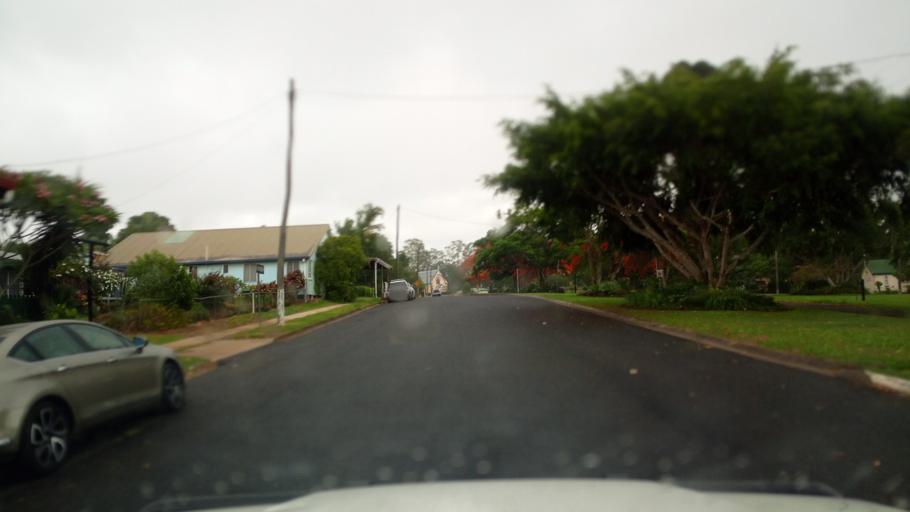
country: AU
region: Queensland
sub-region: Tablelands
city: Tolga
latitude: -17.2696
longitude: 145.5828
